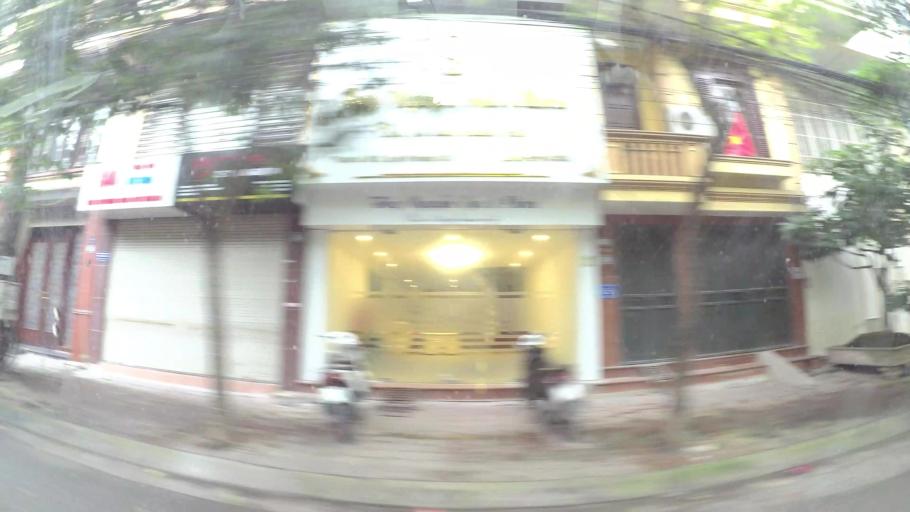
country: VN
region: Ha Noi
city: Dong Da
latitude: 21.0167
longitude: 105.8249
